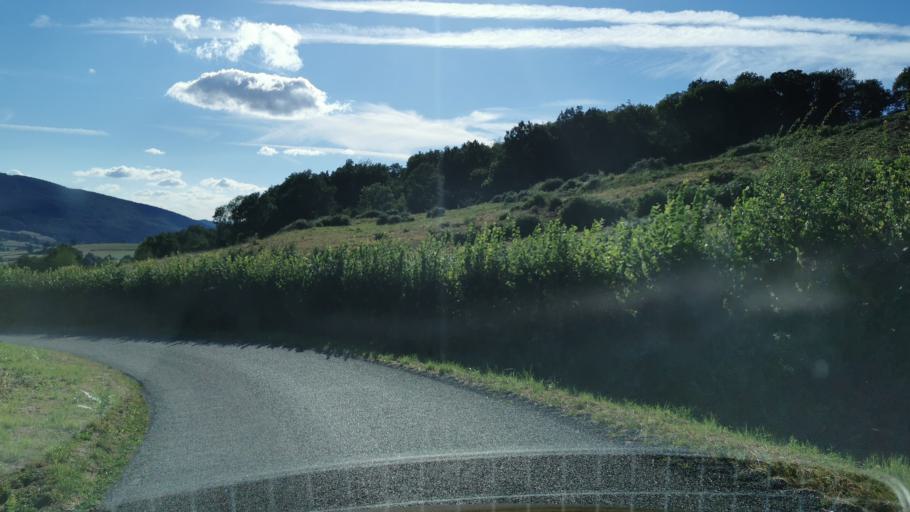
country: FR
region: Bourgogne
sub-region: Departement de Saone-et-Loire
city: Marmagne
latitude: 46.8732
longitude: 4.3350
